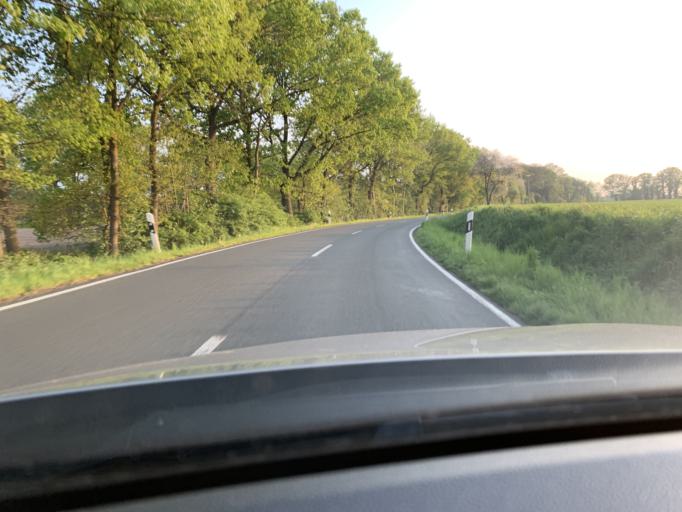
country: DE
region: North Rhine-Westphalia
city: Rietberg
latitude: 51.7814
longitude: 8.4026
